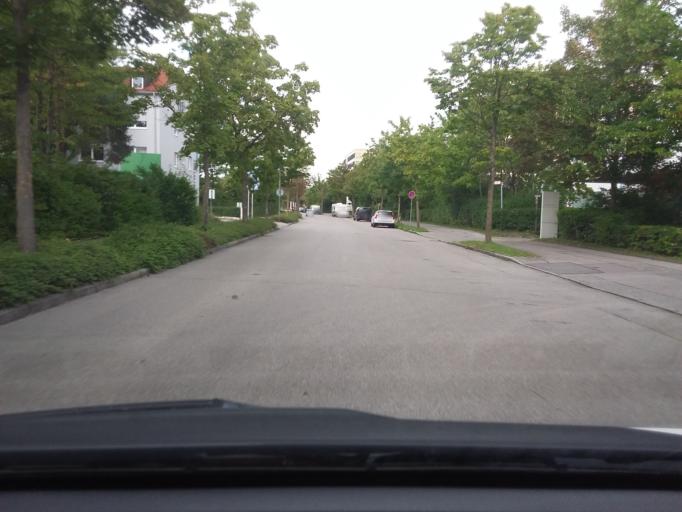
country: DE
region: Bavaria
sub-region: Upper Bavaria
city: Unterschleissheim
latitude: 48.2833
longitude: 11.5717
